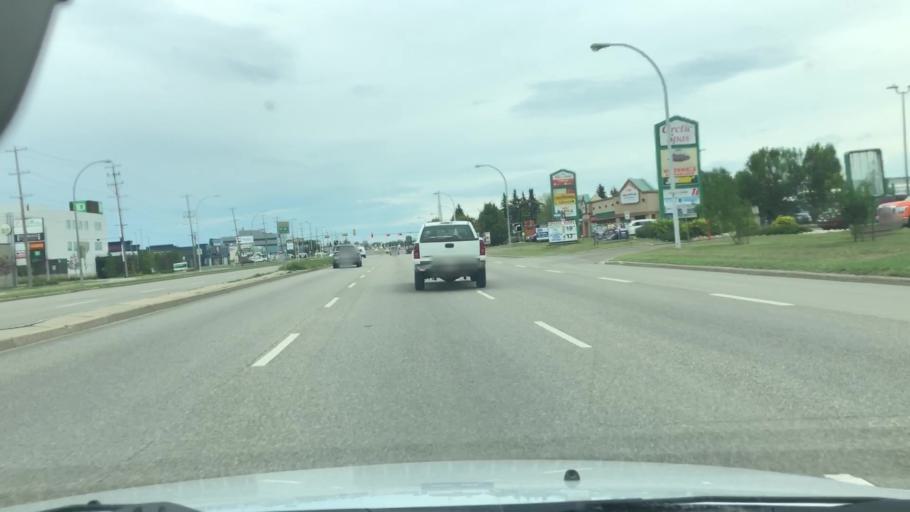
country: CA
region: Alberta
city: St. Albert
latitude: 53.5555
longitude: -113.6154
